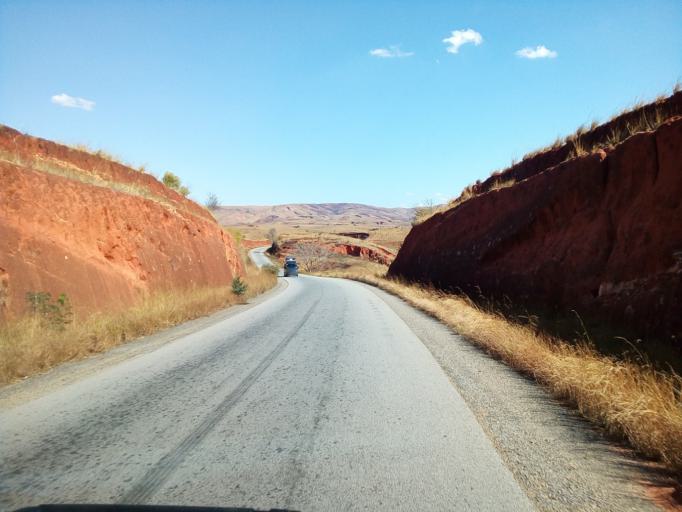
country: MG
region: Betsiboka
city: Maevatanana
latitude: -17.4267
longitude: 46.9423
